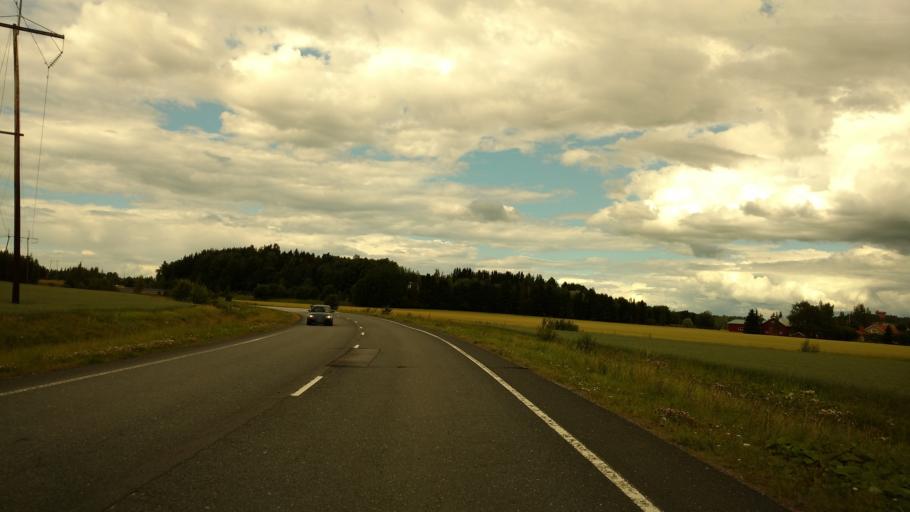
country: FI
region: Varsinais-Suomi
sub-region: Salo
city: Halikko
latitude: 60.3923
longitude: 23.0559
